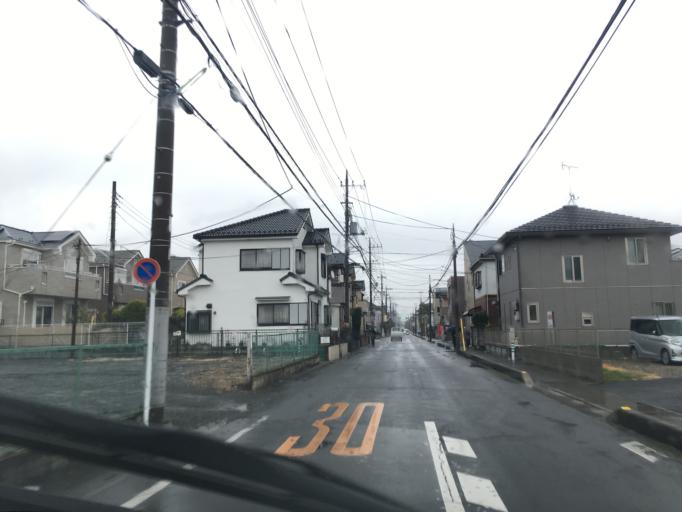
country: JP
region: Saitama
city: Koshigaya
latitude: 35.8861
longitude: 139.7754
